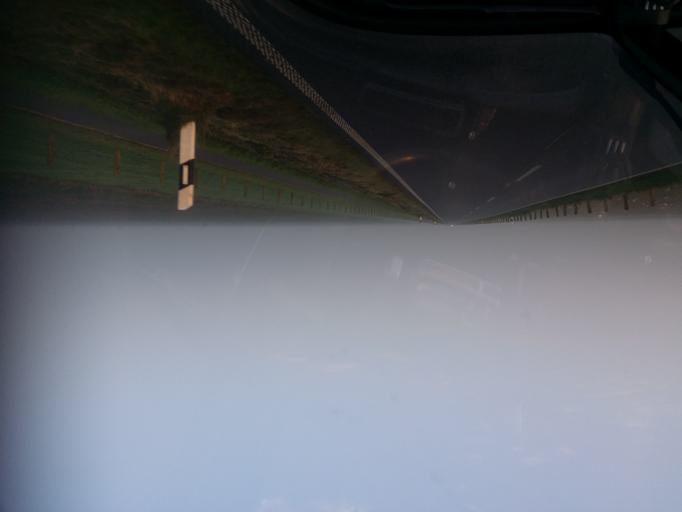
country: DE
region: Schleswig-Holstein
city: Wobbenbull
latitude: 54.5223
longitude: 8.9748
